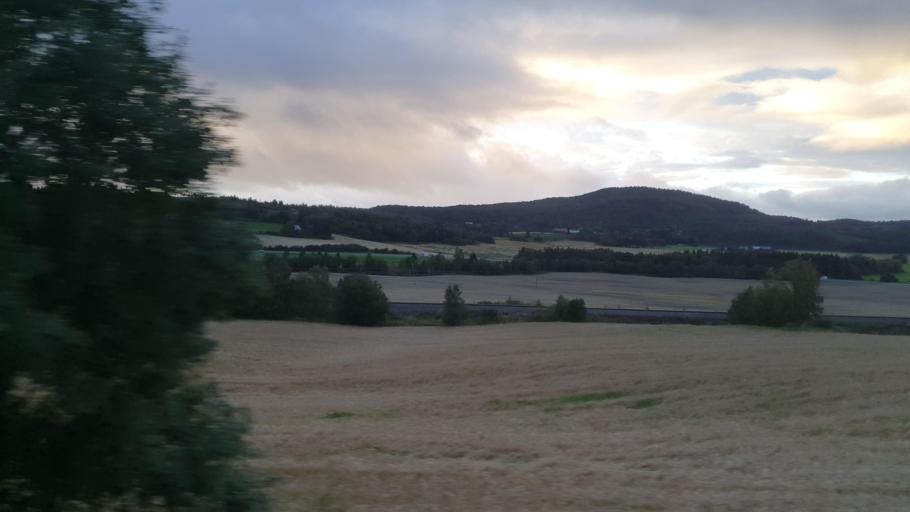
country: NO
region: Nord-Trondelag
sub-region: Levanger
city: Skogn
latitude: 63.6736
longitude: 11.1240
